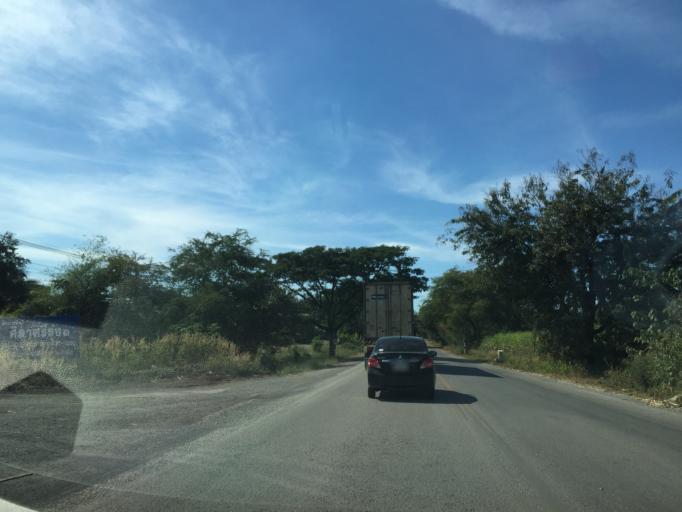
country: TH
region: Changwat Nong Bua Lamphu
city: Na Wang
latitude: 17.3225
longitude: 102.1306
